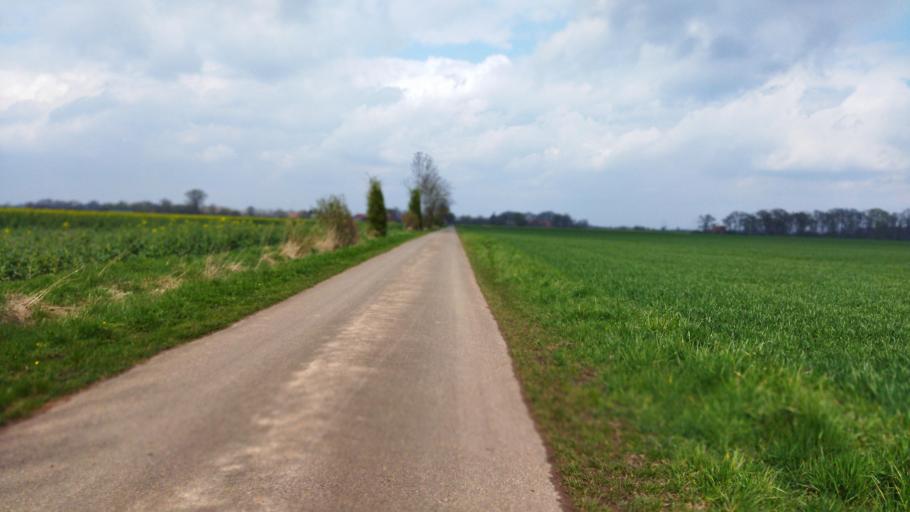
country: DE
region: Lower Saxony
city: Hilgermissen
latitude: 52.8790
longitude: 9.1717
